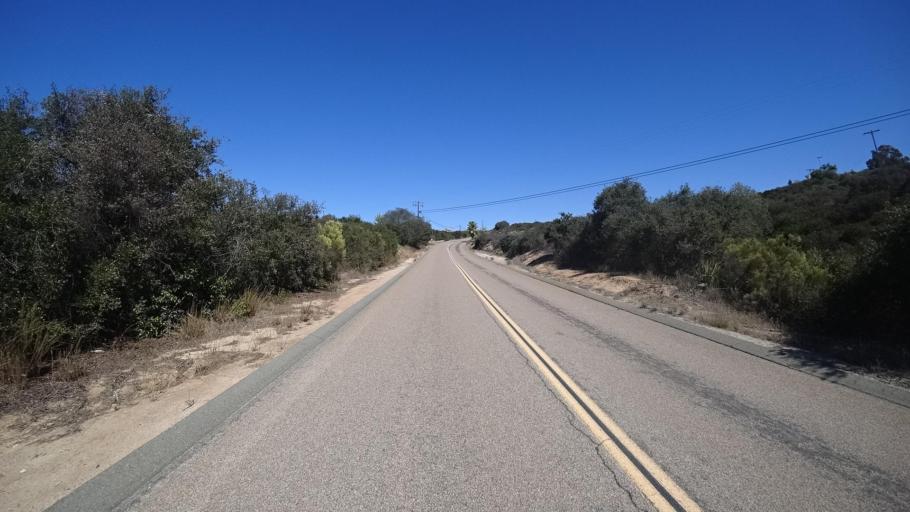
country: US
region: California
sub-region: San Diego County
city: Harbison Canyon
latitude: 32.7910
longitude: -116.8057
